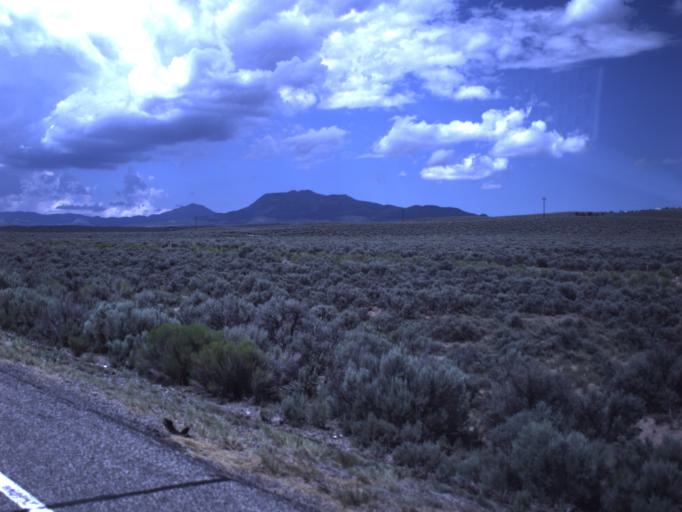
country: US
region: Utah
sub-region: Garfield County
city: Panguitch
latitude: 37.9705
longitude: -112.4093
